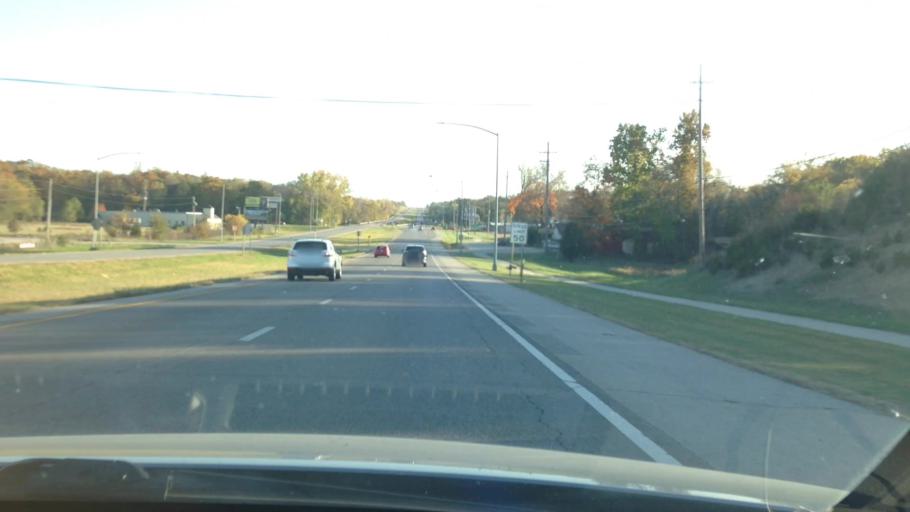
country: US
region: Kansas
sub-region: Leavenworth County
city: Lansing
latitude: 39.2345
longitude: -94.9003
